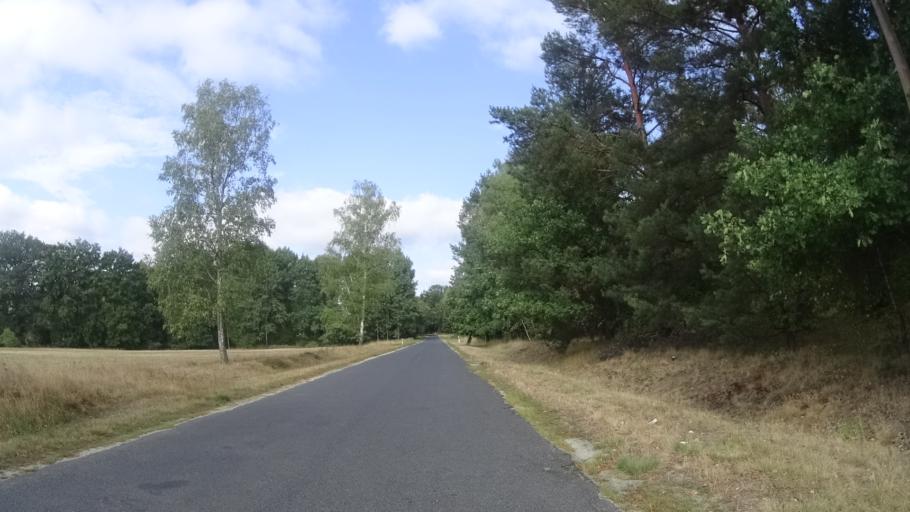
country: PL
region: Lubusz
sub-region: Powiat zarski
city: Przewoz
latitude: 51.4909
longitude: 14.8766
